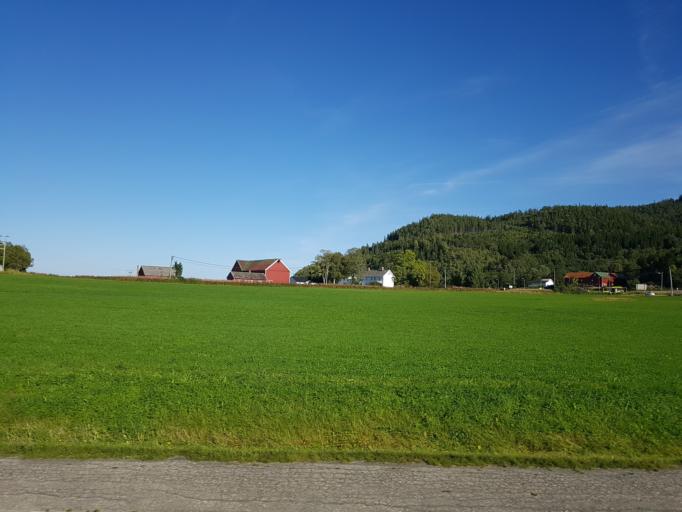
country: NO
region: Sor-Trondelag
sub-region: Skaun
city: Borsa
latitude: 63.4461
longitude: 10.1924
